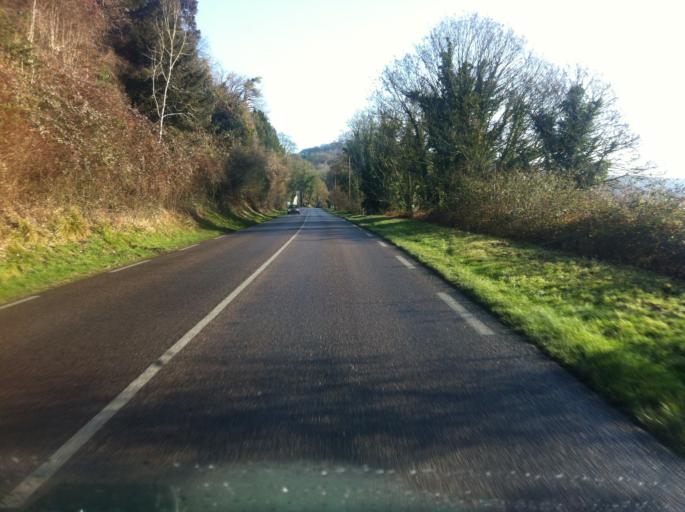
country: FR
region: Haute-Normandie
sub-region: Departement de la Seine-Maritime
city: Saint-Pierre-de-Varengeville
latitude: 49.4854
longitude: 0.9173
